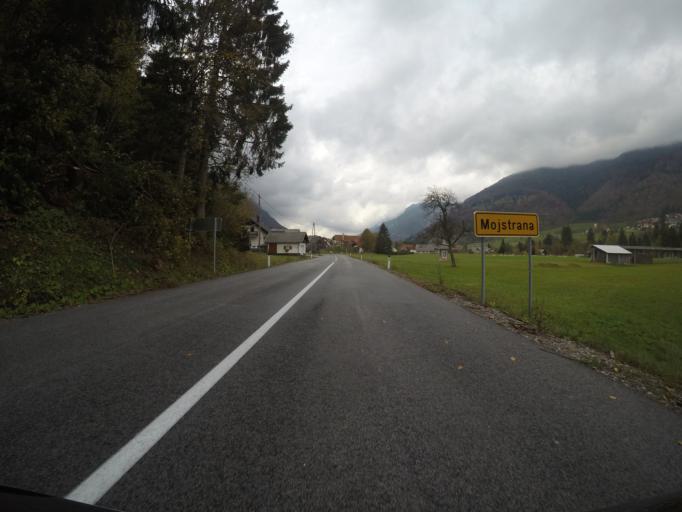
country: SI
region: Jesenice
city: Hrusica
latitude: 46.4598
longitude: 13.9468
